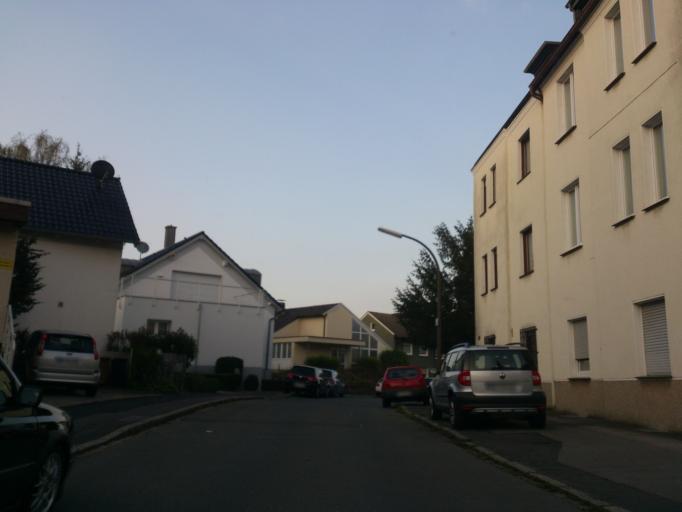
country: DE
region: North Rhine-Westphalia
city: Witten
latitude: 51.4802
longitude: 7.4080
